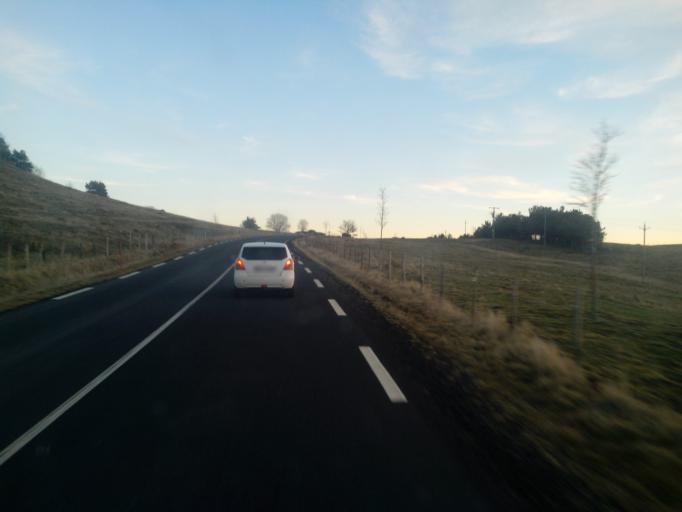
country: FR
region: Auvergne
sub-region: Departement du Cantal
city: Murat
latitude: 45.1483
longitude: 2.8133
